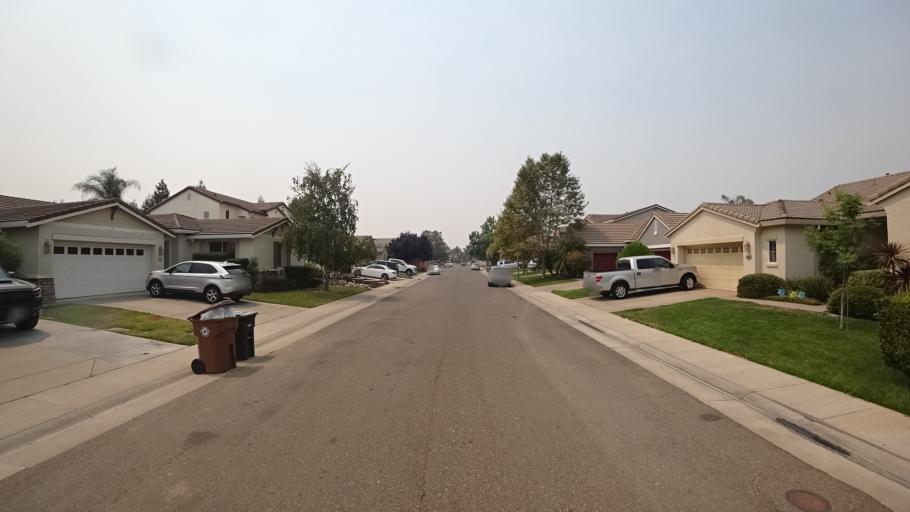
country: US
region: California
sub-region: Sacramento County
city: Laguna
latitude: 38.4004
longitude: -121.4379
